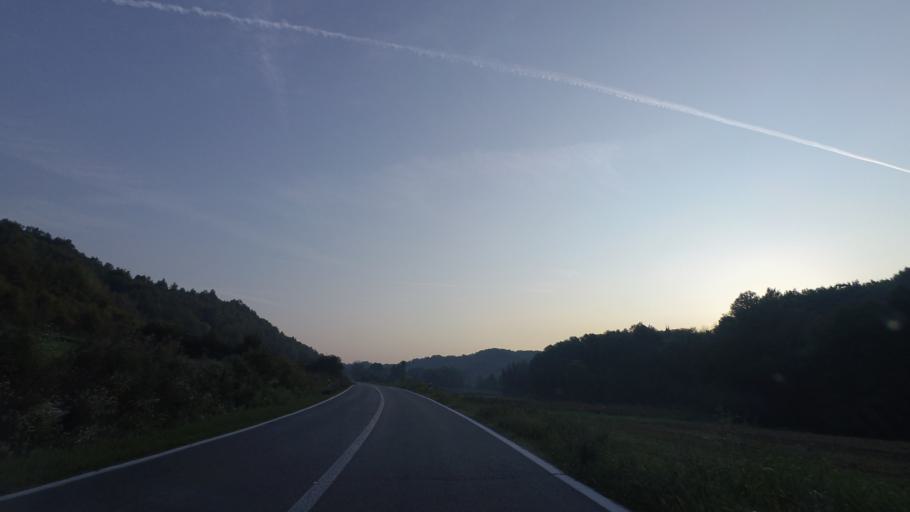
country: HR
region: Brodsko-Posavska
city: Resetari
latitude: 45.3286
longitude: 17.4524
